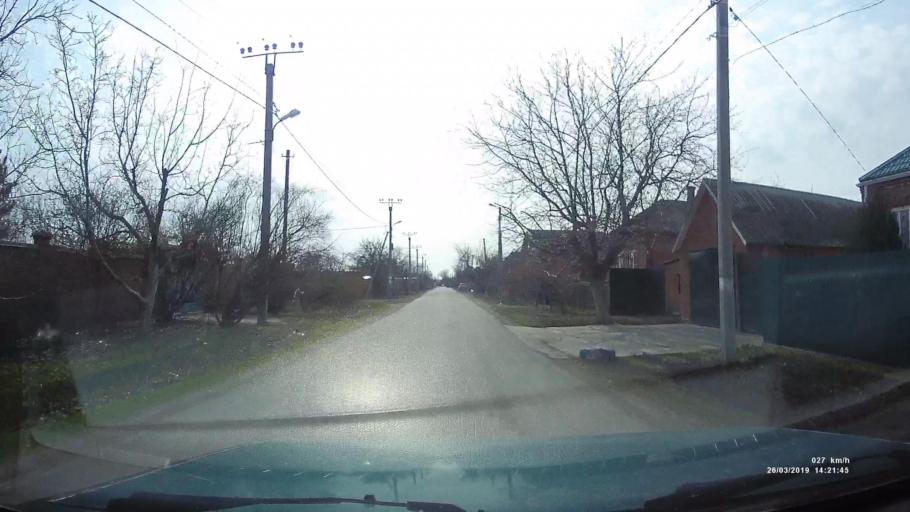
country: RU
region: Rostov
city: Novobessergenovka
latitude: 47.1854
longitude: 38.8674
